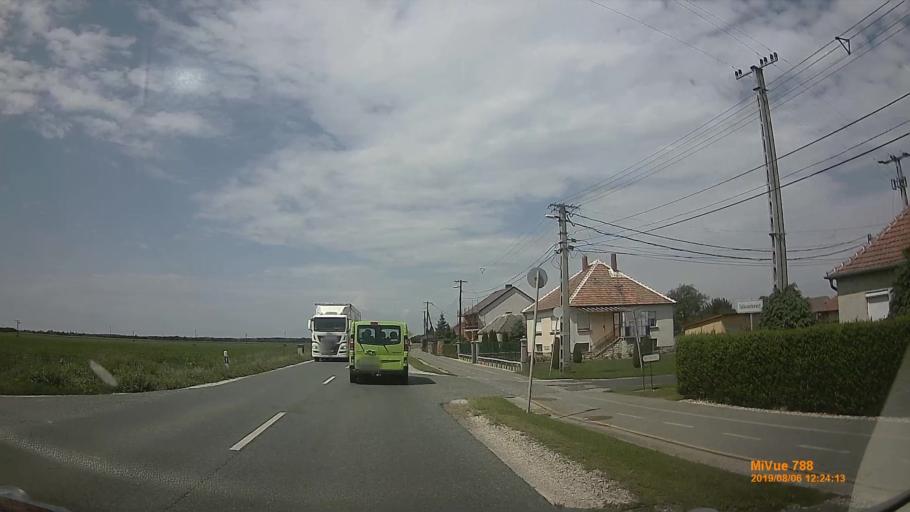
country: HU
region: Vas
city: Taplanszentkereszt
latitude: 47.1918
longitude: 16.7011
